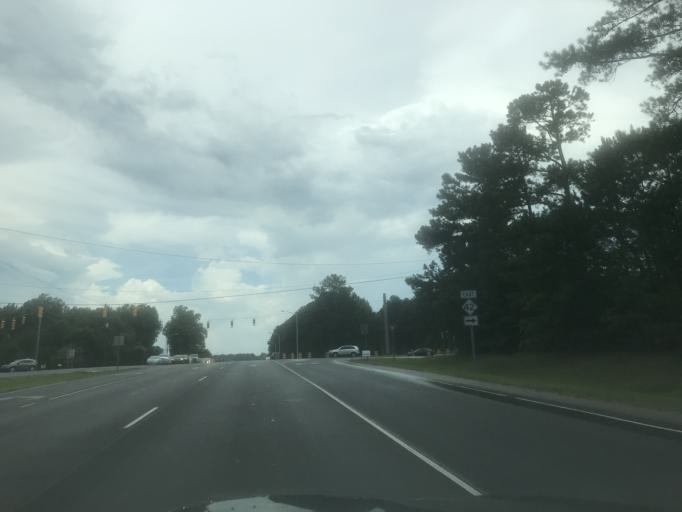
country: US
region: North Carolina
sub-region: Johnston County
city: Clayton
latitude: 35.6362
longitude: -78.4415
